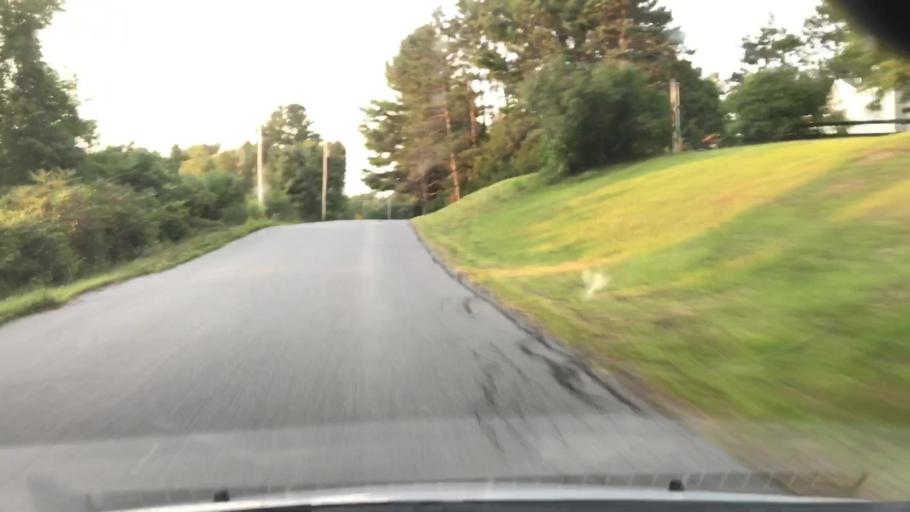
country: US
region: New Hampshire
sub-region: Grafton County
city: North Haverhill
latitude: 44.0728
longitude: -72.0148
